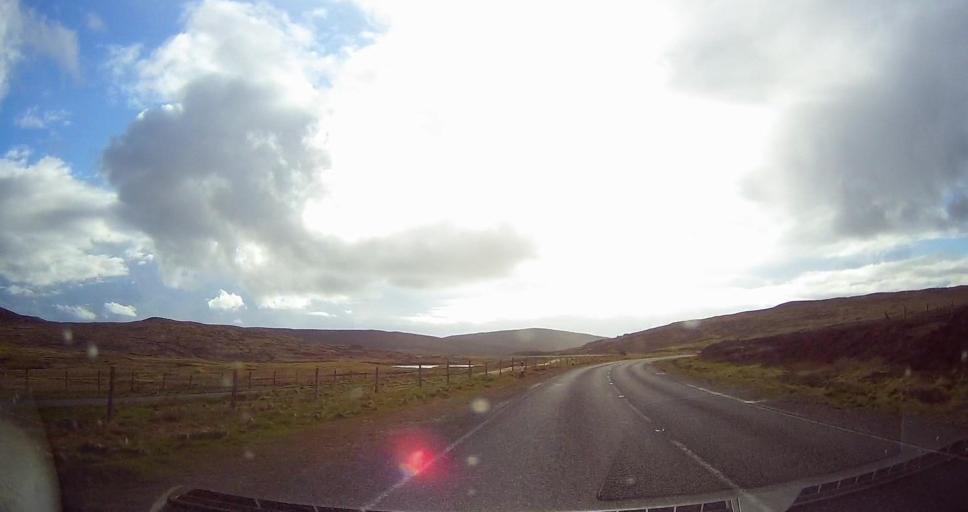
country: GB
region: Scotland
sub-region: Shetland Islands
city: Lerwick
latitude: 60.3486
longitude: -1.2249
